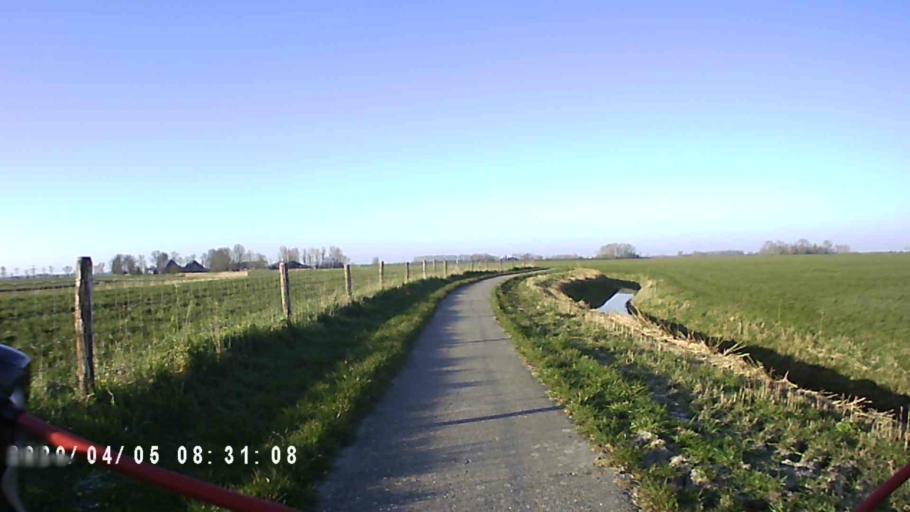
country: NL
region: Groningen
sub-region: Gemeente Winsum
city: Winsum
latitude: 53.3315
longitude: 6.4848
